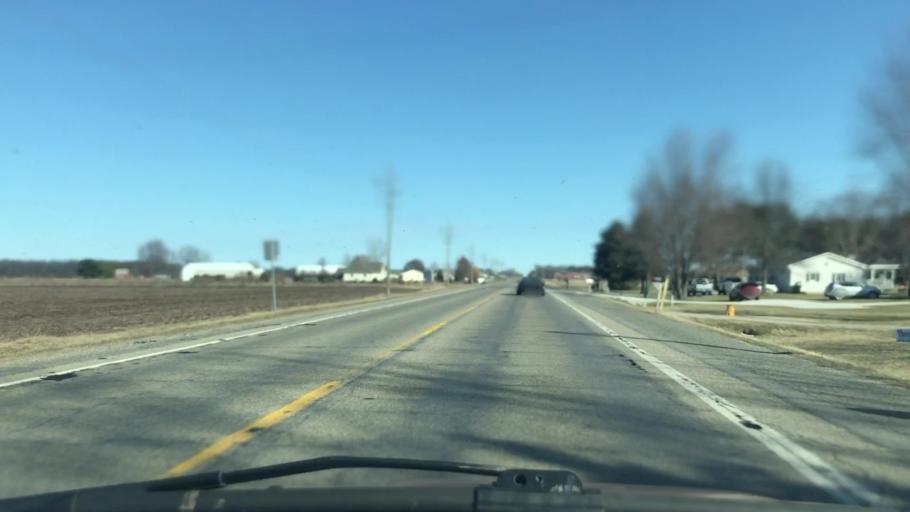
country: US
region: Indiana
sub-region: Porter County
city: Kouts
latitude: 41.3822
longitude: -87.0270
